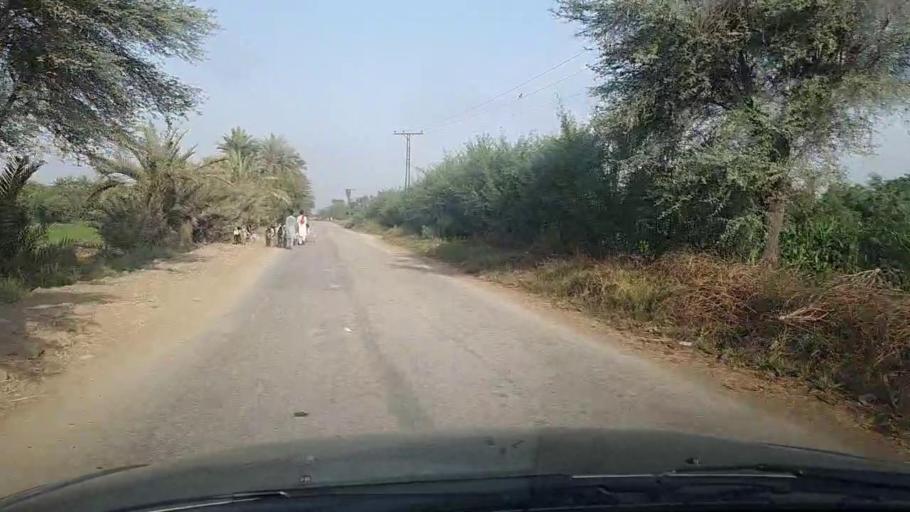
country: PK
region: Sindh
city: Pir jo Goth
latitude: 27.5712
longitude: 68.6014
